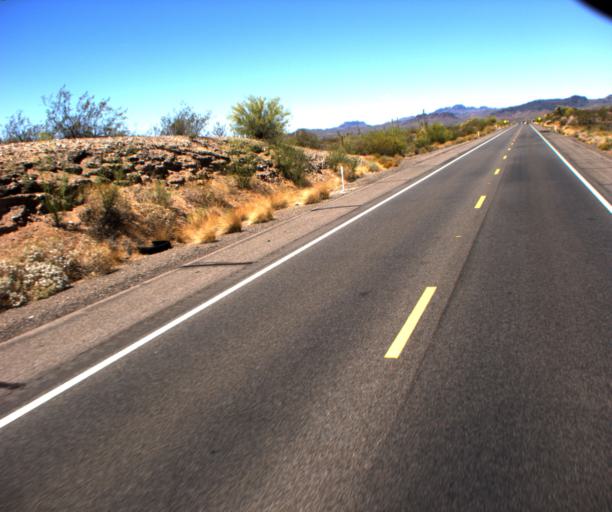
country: US
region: Arizona
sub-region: Maricopa County
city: Wickenburg
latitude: 33.8634
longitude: -112.6203
